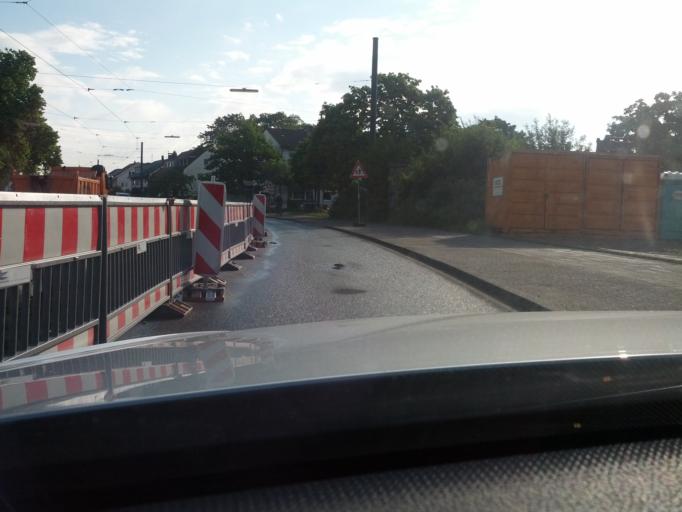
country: DE
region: Baden-Wuerttemberg
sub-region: Karlsruhe Region
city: Karlsruhe
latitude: 49.0116
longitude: 8.4391
